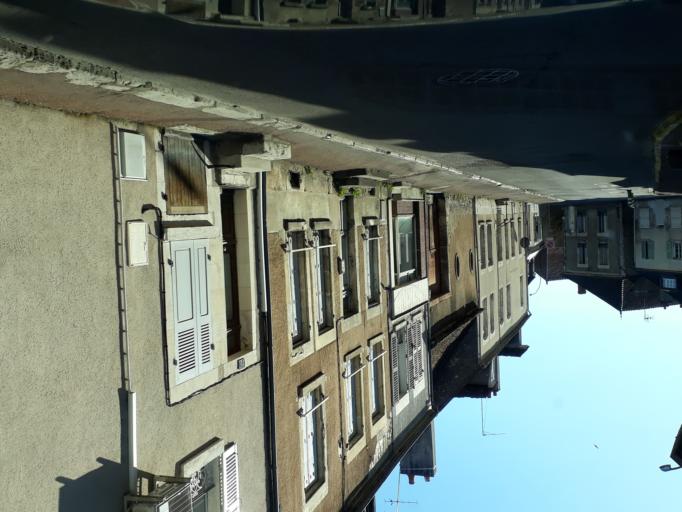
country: FR
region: Bourgogne
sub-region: Departement de la Nievre
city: Cosne-Cours-sur-Loire
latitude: 47.4107
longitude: 2.9233
